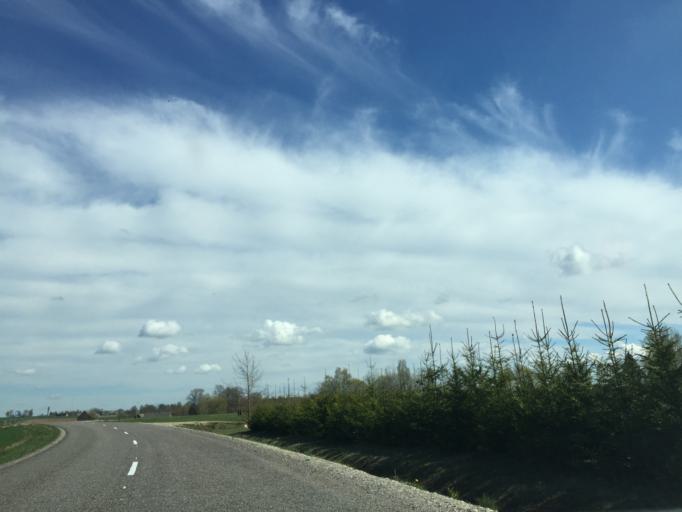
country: LV
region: Strenci
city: Strenci
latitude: 57.5517
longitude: 25.6764
